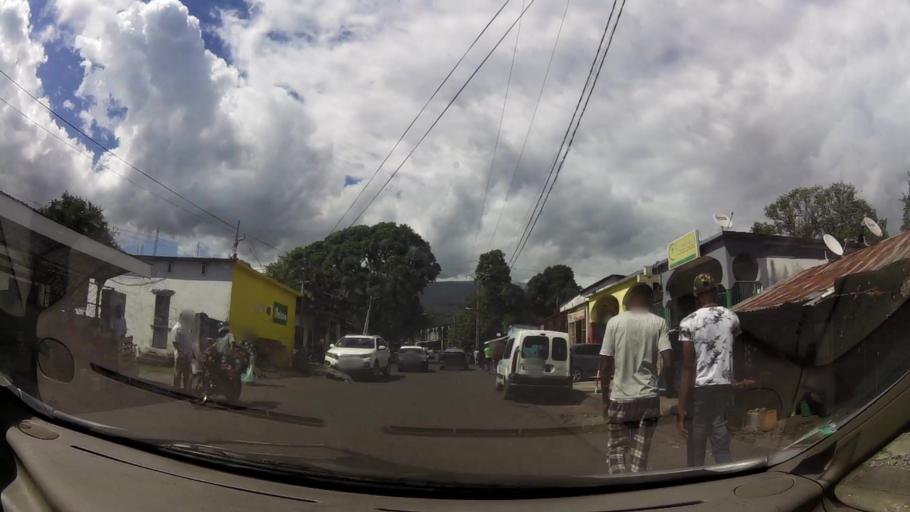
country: KM
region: Grande Comore
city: Mavingouni
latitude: -11.7098
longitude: 43.2498
